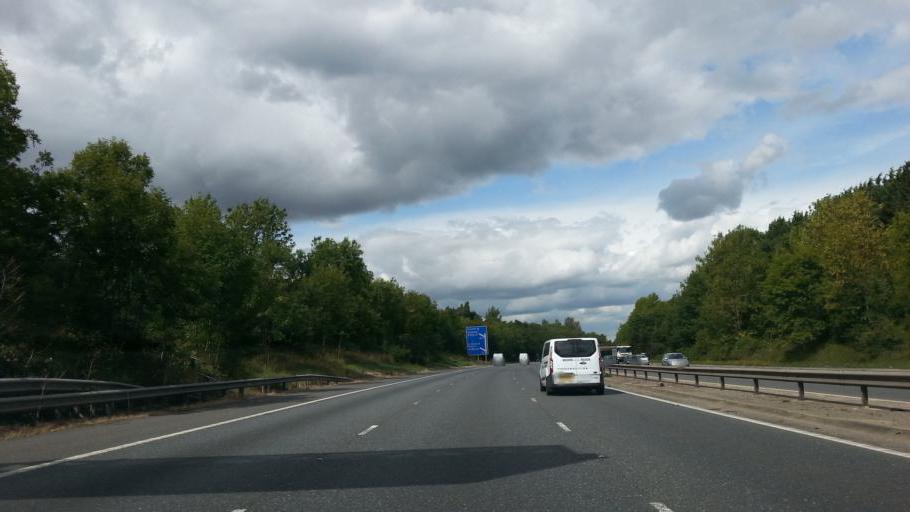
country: GB
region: England
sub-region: Essex
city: Little Hallingbury
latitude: 51.8456
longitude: 0.1869
